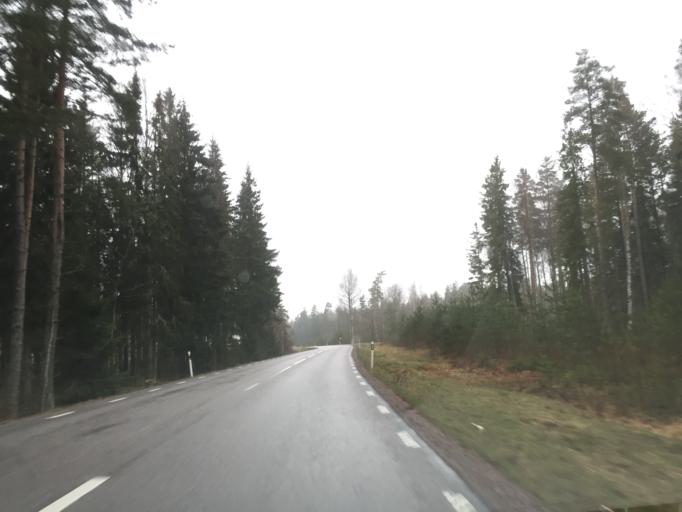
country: SE
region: OErebro
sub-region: Hallsbergs Kommun
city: Skollersta
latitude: 59.2438
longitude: 15.4000
